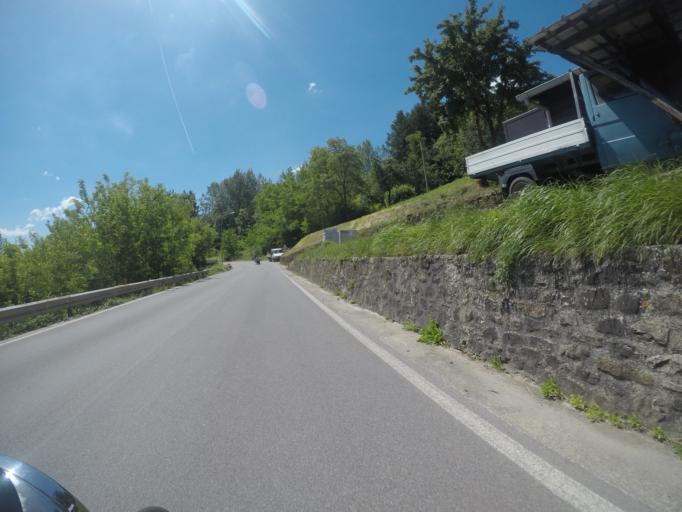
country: IT
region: Tuscany
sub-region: Provincia di Lucca
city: Villa Collemandina
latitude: 44.1324
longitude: 10.3741
